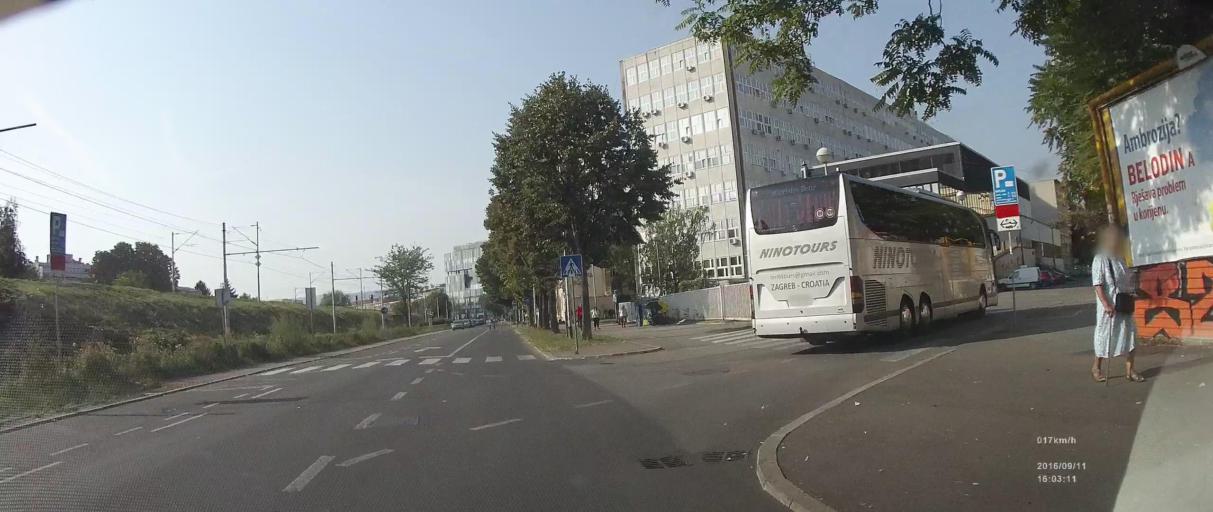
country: HR
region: Grad Zagreb
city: Zagreb - Centar
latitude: 45.8060
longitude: 15.9644
